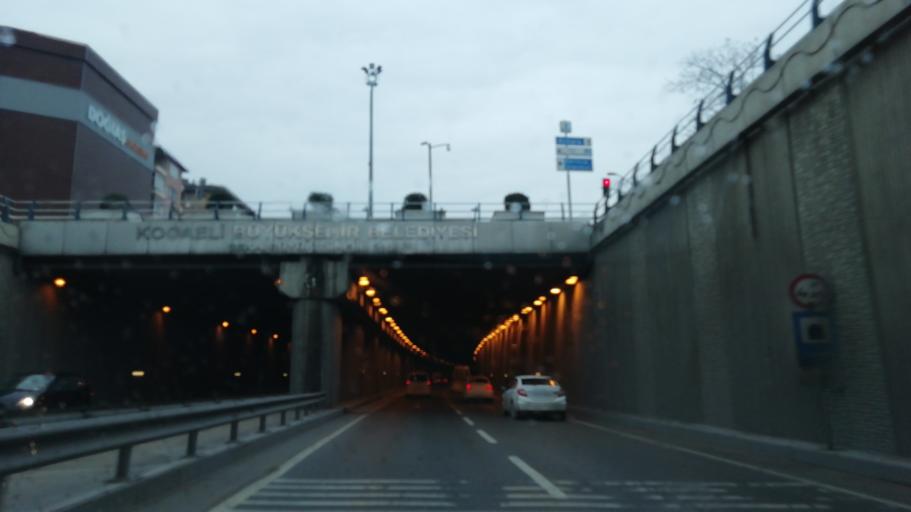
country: TR
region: Kocaeli
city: Izmit
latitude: 40.7660
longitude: 29.9091
